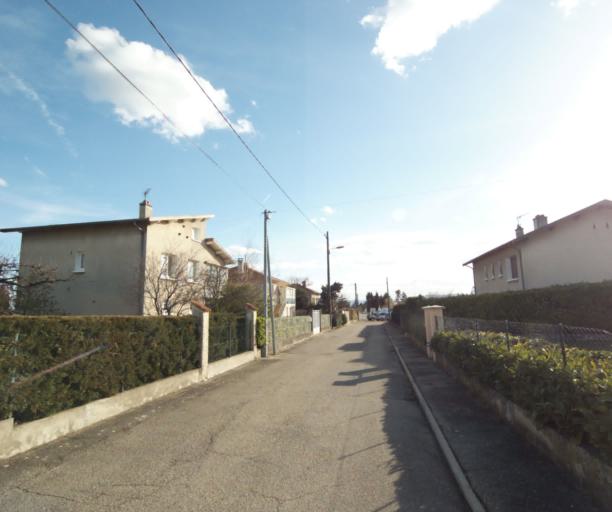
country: FR
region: Rhone-Alpes
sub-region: Departement de l'Ardeche
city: Davezieux
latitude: 45.2565
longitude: 4.6982
